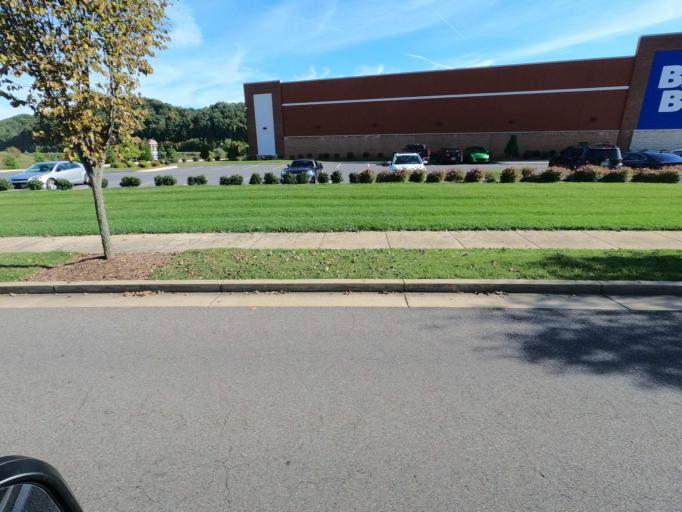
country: US
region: Tennessee
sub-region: Sullivan County
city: Walnut Hill
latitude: 36.5932
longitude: -82.2559
